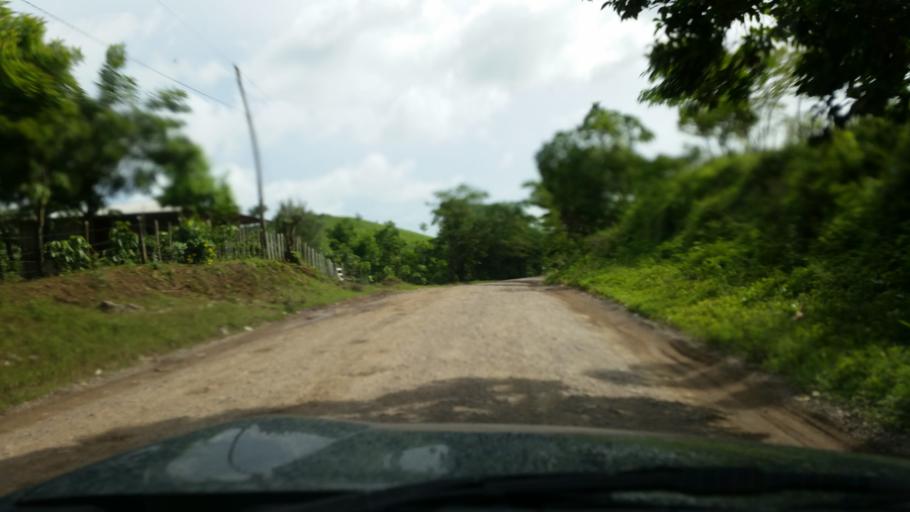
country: NI
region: Atlantico Norte (RAAN)
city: Siuna
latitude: 13.5990
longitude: -84.8017
